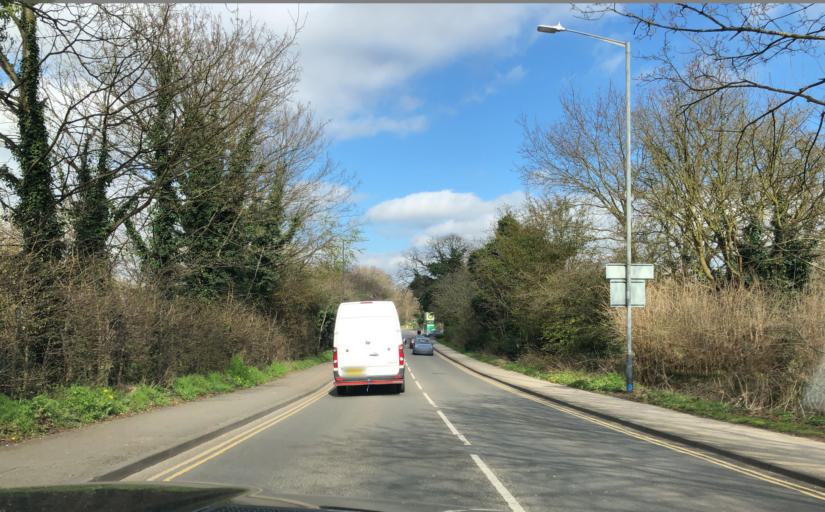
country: GB
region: England
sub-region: Warwickshire
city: Warwick
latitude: 52.2912
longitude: -1.5779
